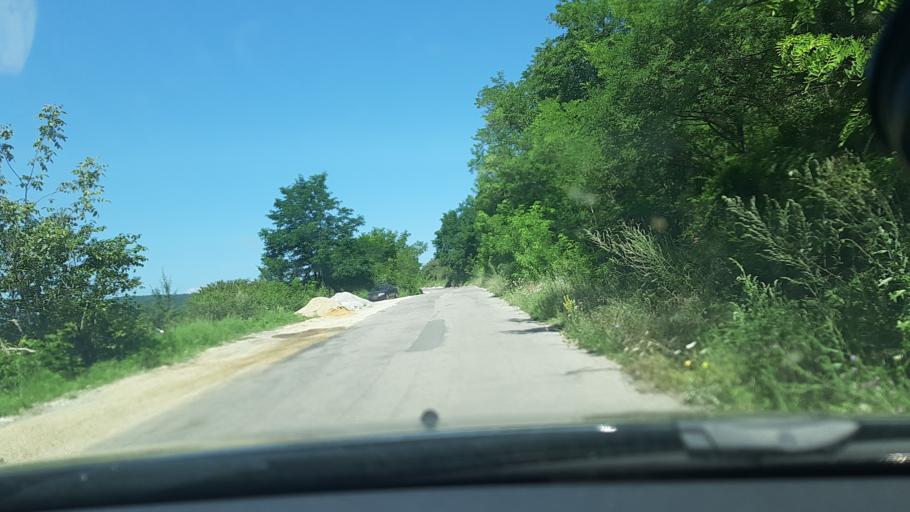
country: RO
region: Hunedoara
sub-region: Comuna Teliucu Inferior
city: Teliucu Inferior
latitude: 45.6885
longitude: 22.8765
